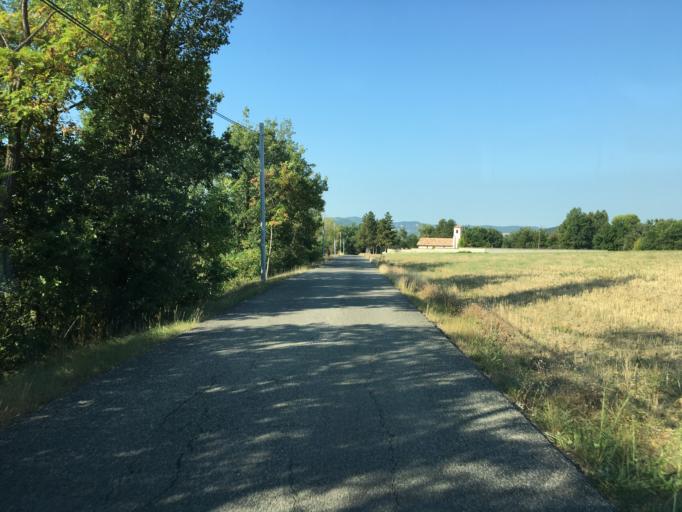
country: FR
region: Provence-Alpes-Cote d'Azur
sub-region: Departement des Alpes-de-Haute-Provence
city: Mallemoisson
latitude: 44.0529
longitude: 6.1515
